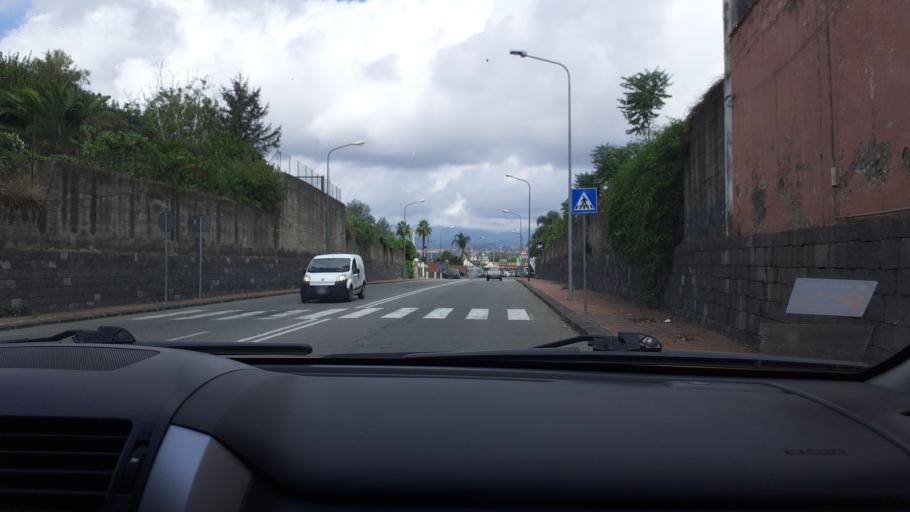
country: IT
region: Sicily
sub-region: Catania
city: San Gregorio di Catania
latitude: 37.5643
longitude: 15.1064
